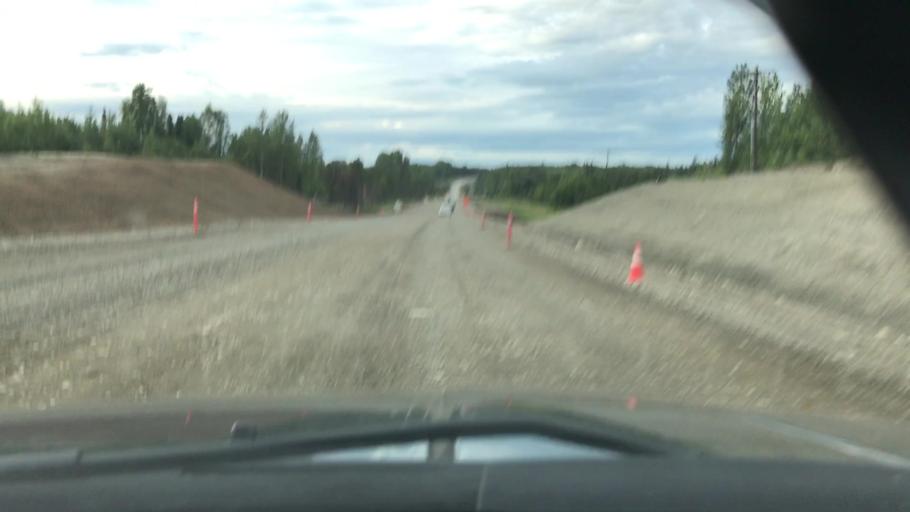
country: US
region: Alaska
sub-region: Matanuska-Susitna Borough
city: Y
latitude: 62.0956
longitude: -150.0618
